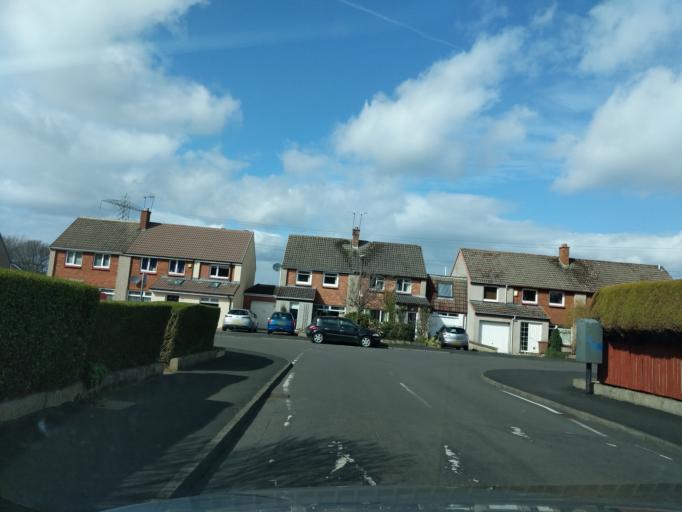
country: GB
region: Scotland
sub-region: Edinburgh
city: Currie
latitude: 55.9016
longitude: -3.3045
